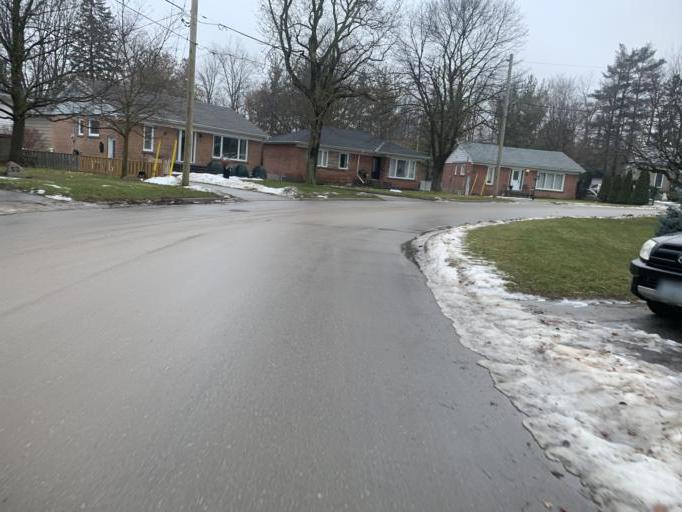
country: CA
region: Ontario
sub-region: Halton
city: Milton
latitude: 43.6552
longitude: -79.9263
